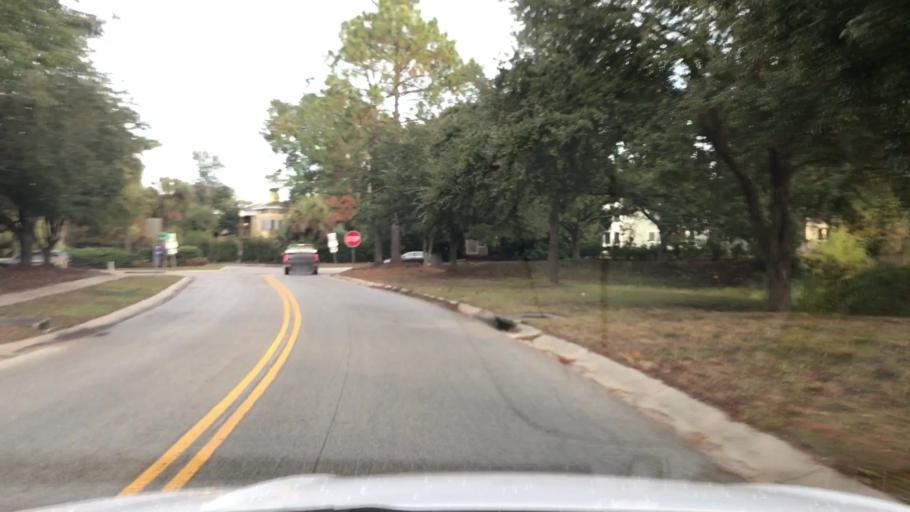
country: US
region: South Carolina
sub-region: Charleston County
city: Mount Pleasant
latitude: 32.8041
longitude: -79.8956
